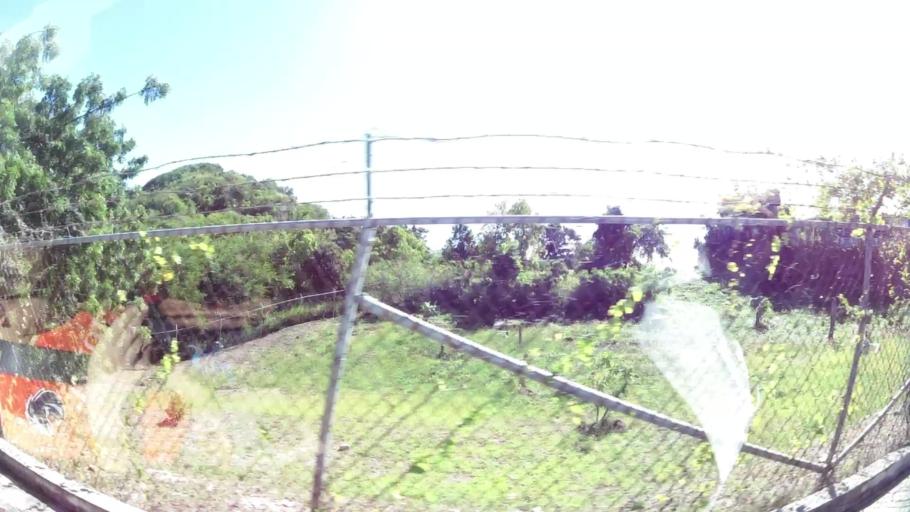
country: AG
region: Saint Paul
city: Falmouth
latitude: 17.0237
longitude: -61.7451
